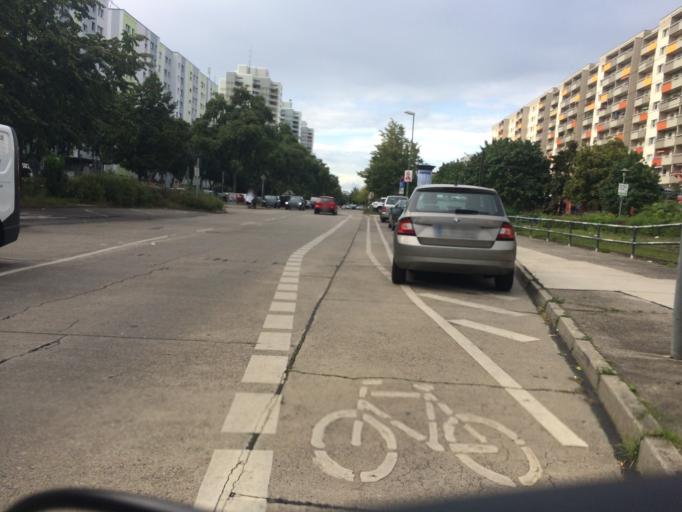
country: DE
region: Berlin
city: Neu-Hohenschoenhausen
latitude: 52.5638
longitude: 13.5044
